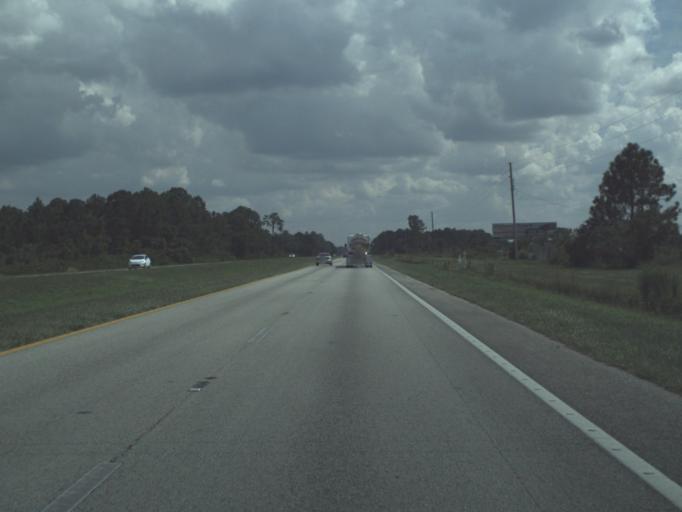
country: US
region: Florida
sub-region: Polk County
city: Frostproof
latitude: 27.7514
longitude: -81.5852
